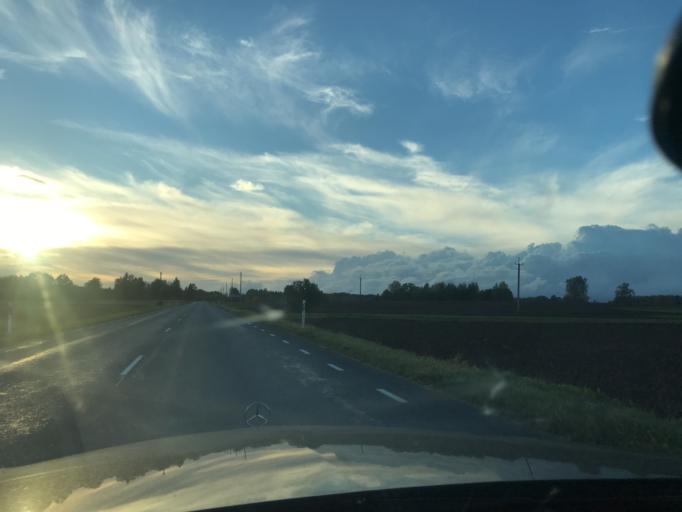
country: EE
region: Vorumaa
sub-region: Antsla vald
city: Vana-Antsla
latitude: 57.8798
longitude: 26.7128
